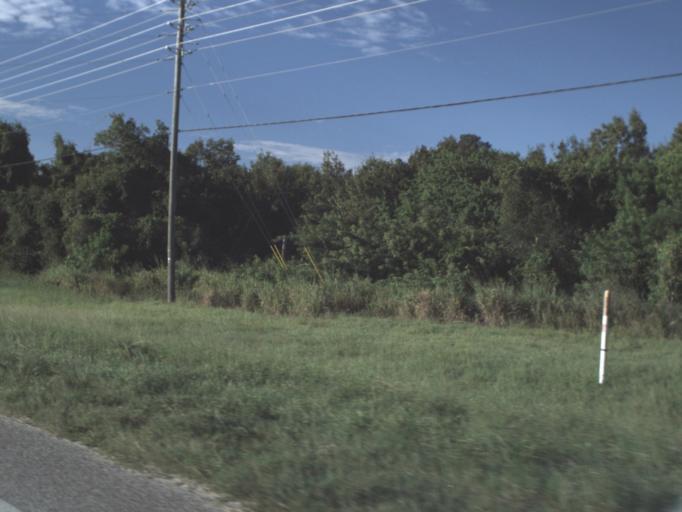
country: US
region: Florida
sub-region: Highlands County
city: Lake Placid
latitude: 27.2853
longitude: -81.3574
